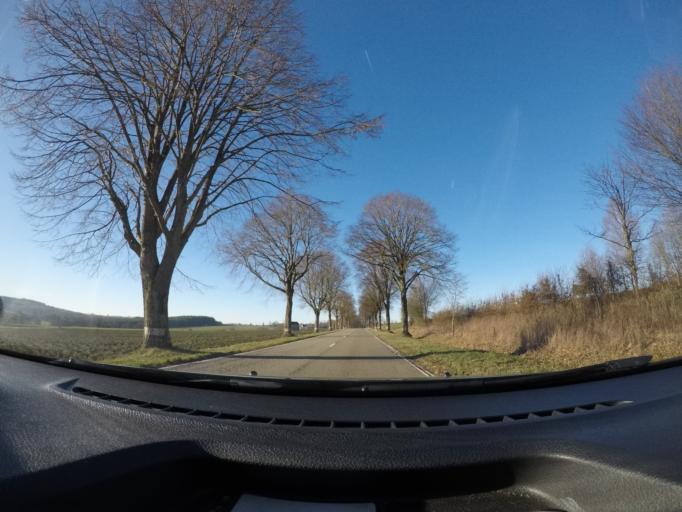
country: BE
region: Wallonia
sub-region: Province du Luxembourg
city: Bertrix
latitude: 49.8499
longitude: 5.2966
